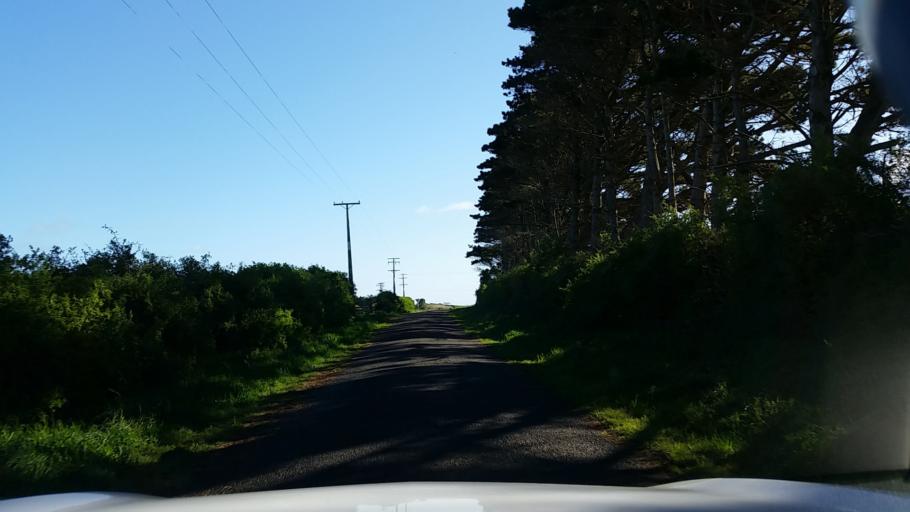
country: NZ
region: Taranaki
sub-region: South Taranaki District
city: Hawera
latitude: -39.6669
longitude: 174.3849
